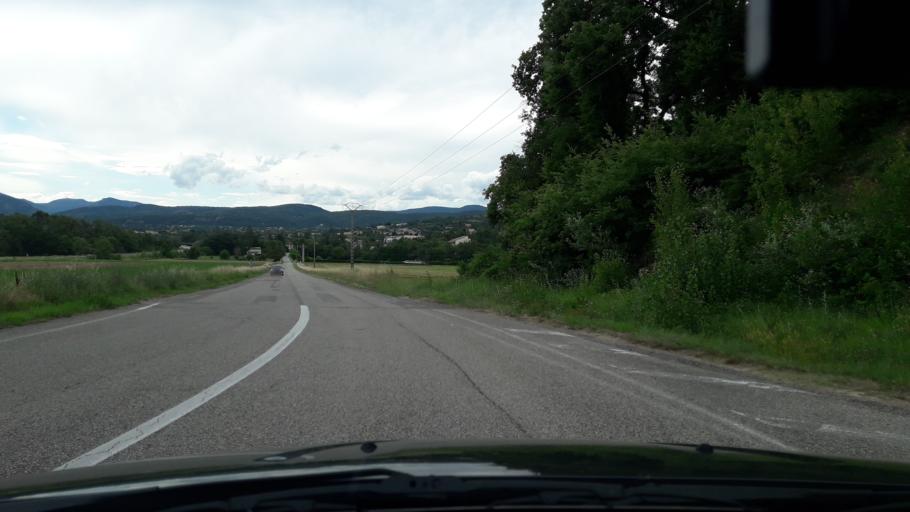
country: FR
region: Rhone-Alpes
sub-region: Departement de l'Ardeche
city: Le Pouzin
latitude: 44.7097
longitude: 4.7221
